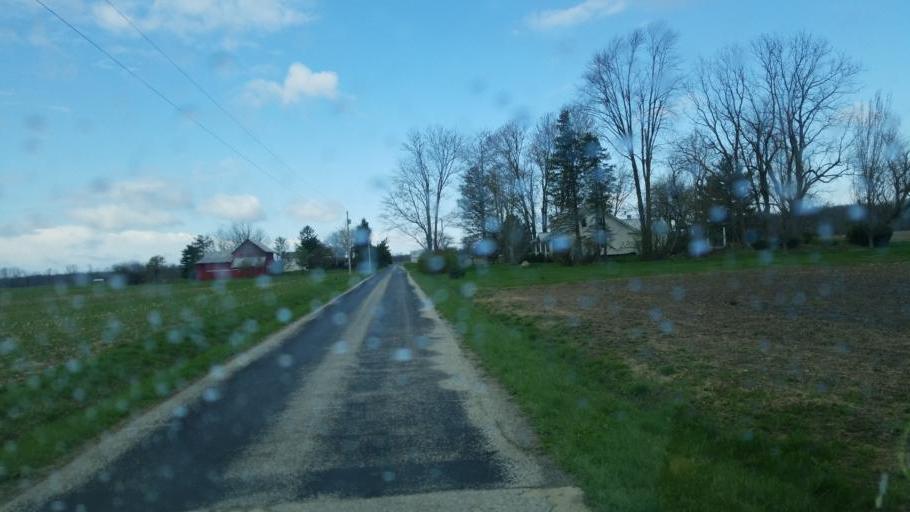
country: US
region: Ohio
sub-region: Delaware County
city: Ashley
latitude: 40.3895
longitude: -83.0169
